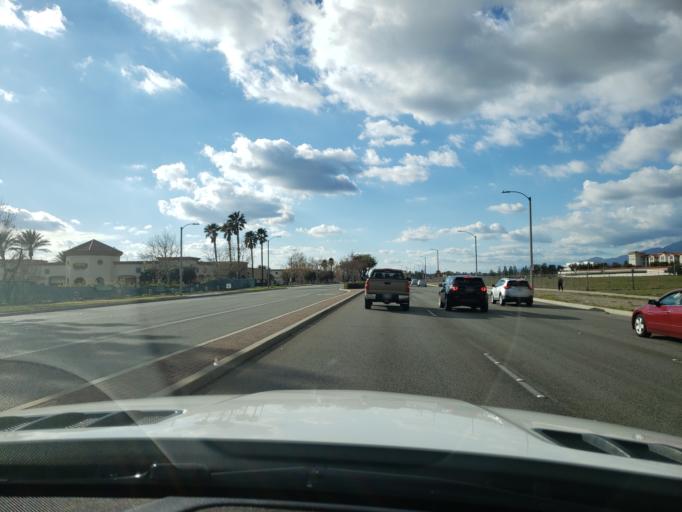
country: US
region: California
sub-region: San Bernardino County
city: Rancho Cucamonga
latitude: 34.1064
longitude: -117.5497
